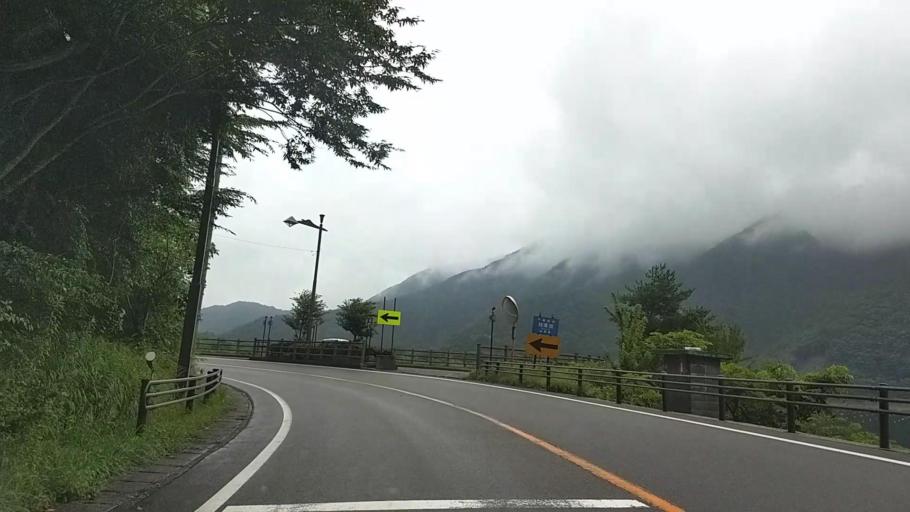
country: JP
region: Yamanashi
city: Fujikawaguchiko
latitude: 35.4923
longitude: 138.6107
